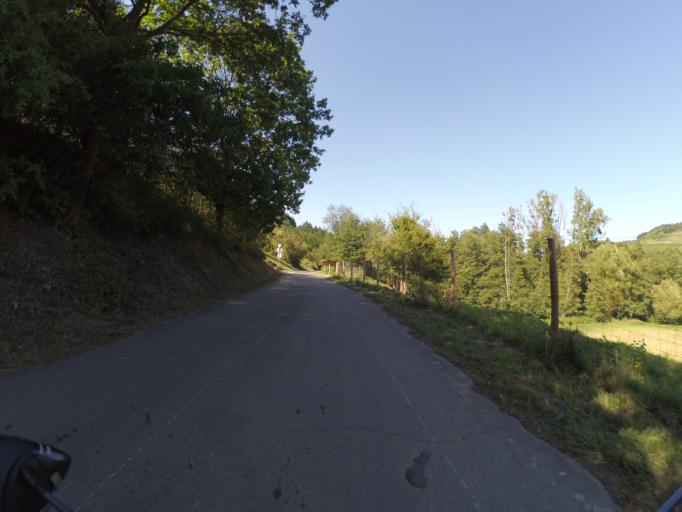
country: DE
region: Rheinland-Pfalz
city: Thornich
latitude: 49.8481
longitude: 6.8384
